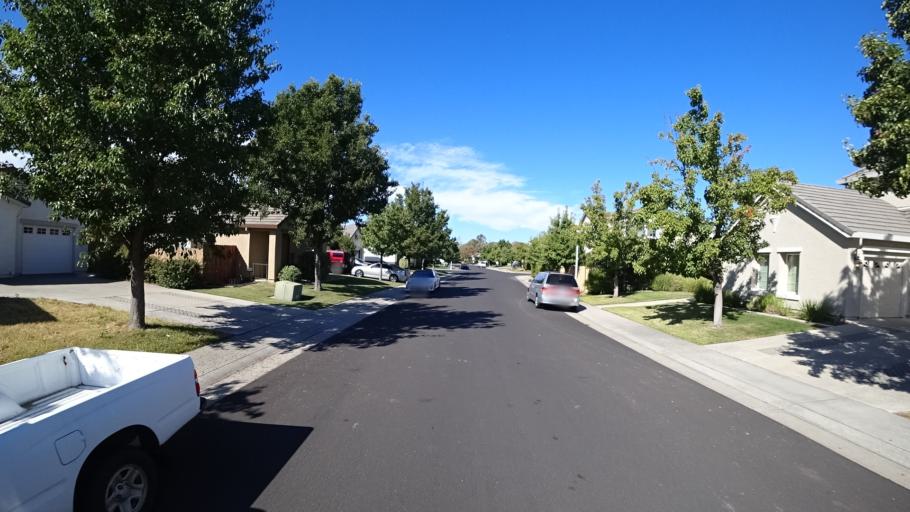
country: US
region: California
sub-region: Sacramento County
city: Laguna
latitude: 38.4244
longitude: -121.4785
